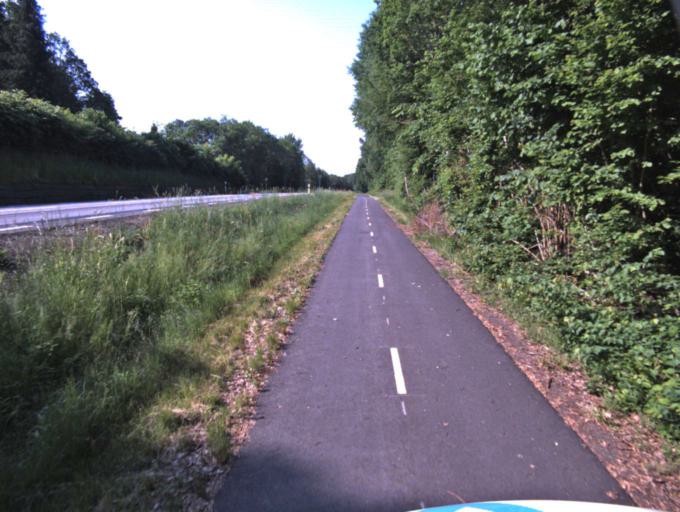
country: SE
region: Skane
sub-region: Kristianstads Kommun
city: Tollarp
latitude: 56.1562
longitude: 14.2682
